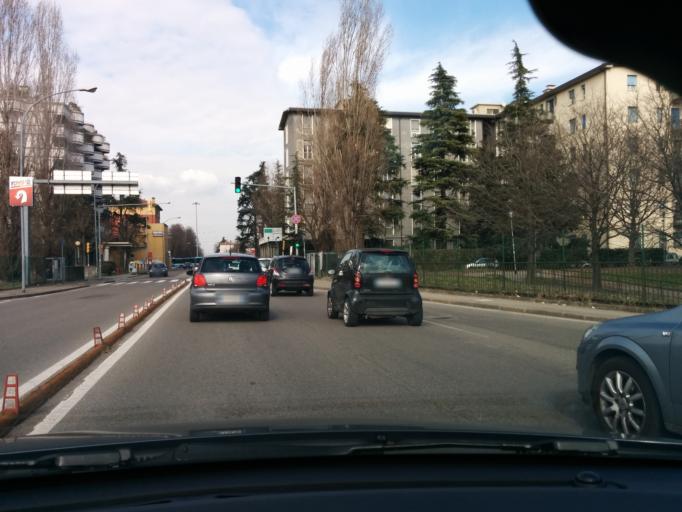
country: IT
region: Emilia-Romagna
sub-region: Provincia di Bologna
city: Bologna
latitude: 44.5156
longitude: 11.3280
